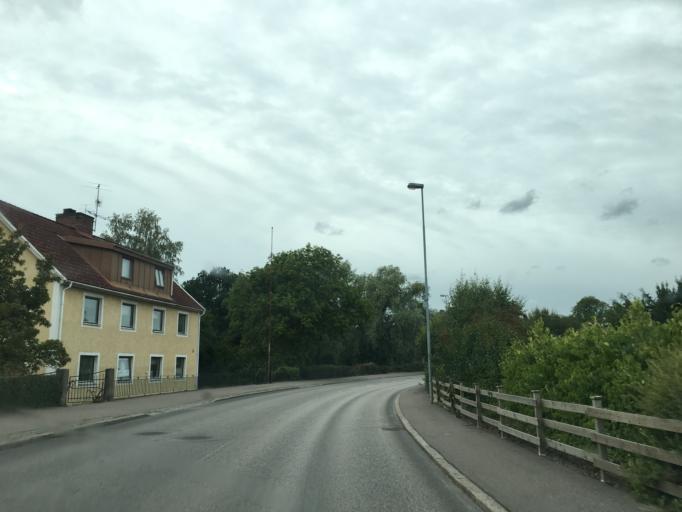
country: SE
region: Kalmar
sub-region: Nybro Kommun
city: Nybro
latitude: 56.7413
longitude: 15.9183
